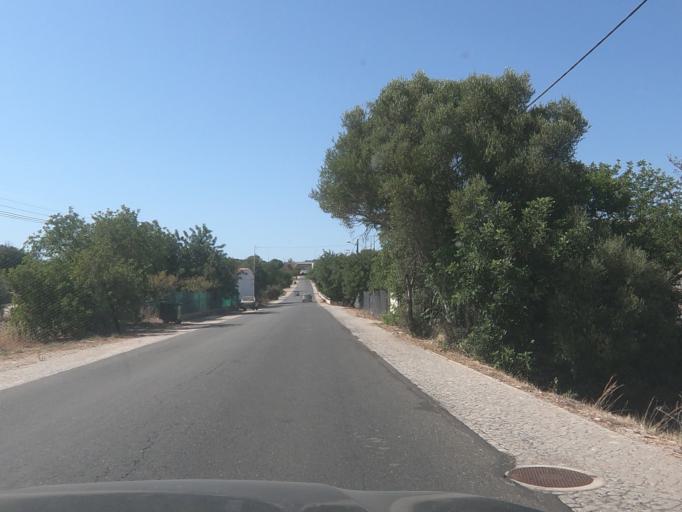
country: PT
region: Faro
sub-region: Faro
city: Santa Barbara de Nexe
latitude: 37.0889
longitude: -7.9924
